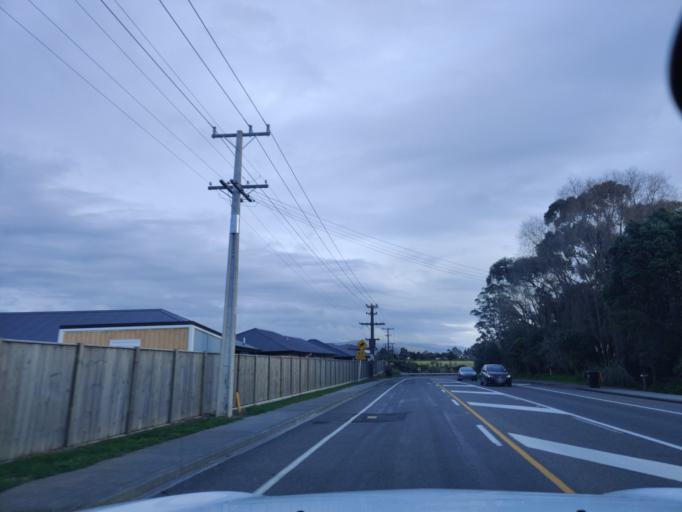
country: NZ
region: Manawatu-Wanganui
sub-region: Palmerston North City
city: Palmerston North
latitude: -40.3847
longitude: 175.6466
